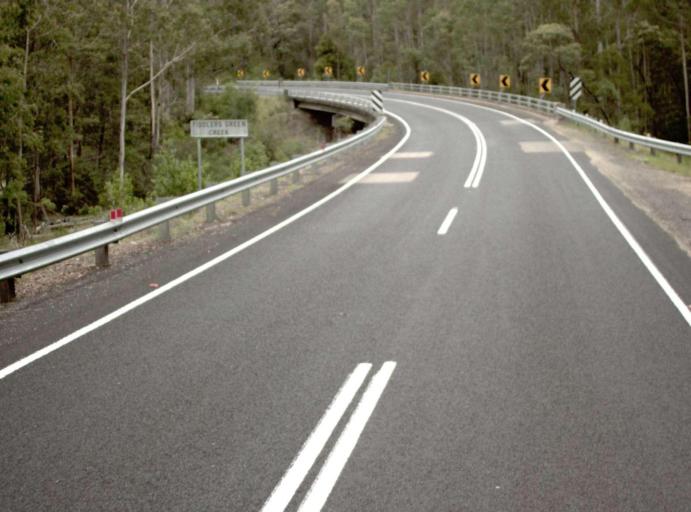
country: AU
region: New South Wales
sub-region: Bombala
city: Bombala
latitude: -37.2946
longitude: 149.2144
